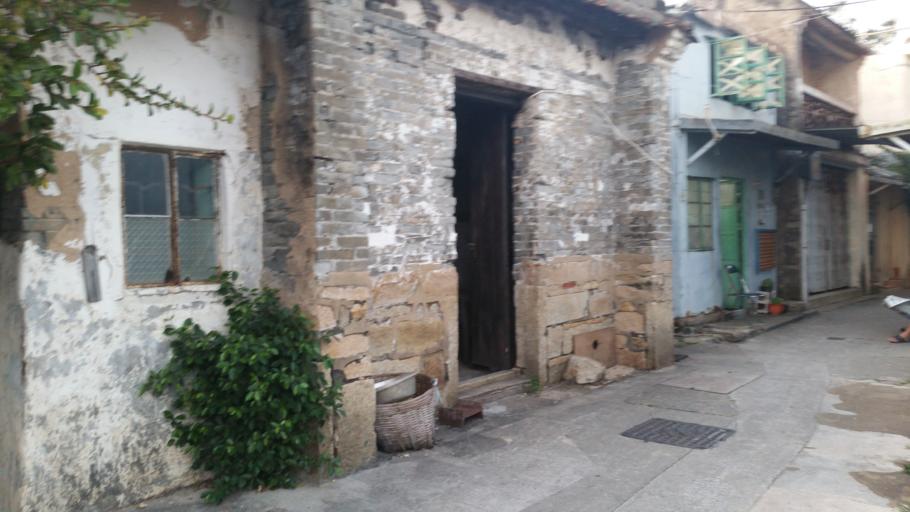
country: HK
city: Tai O
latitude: 22.2539
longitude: 113.8605
